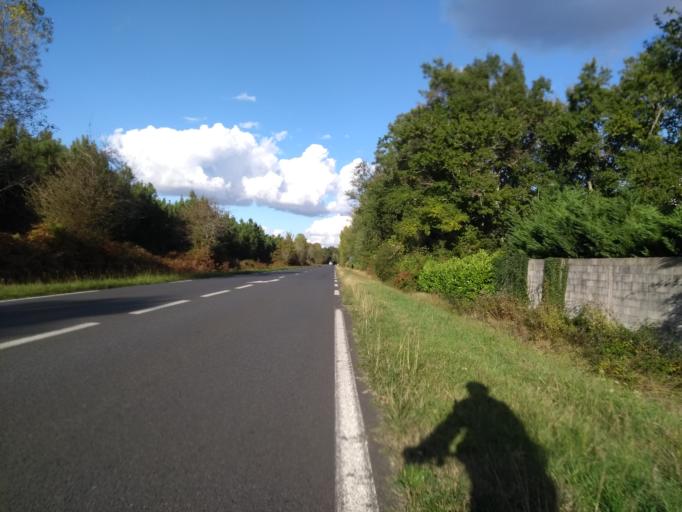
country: FR
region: Aquitaine
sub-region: Departement de la Gironde
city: Cestas
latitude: 44.7183
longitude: -0.6892
